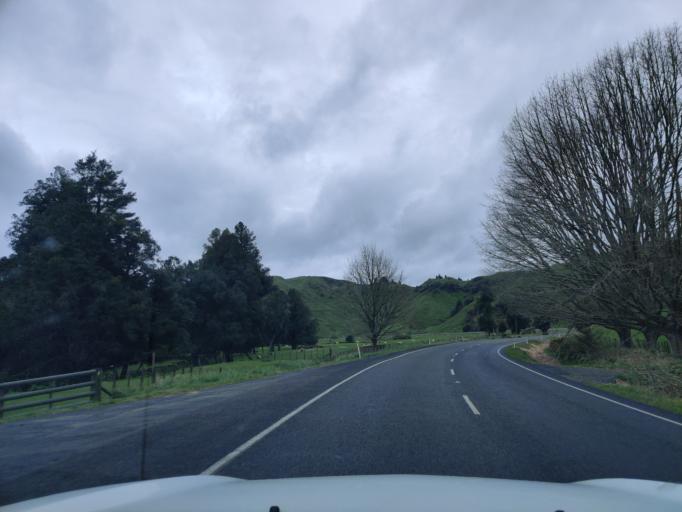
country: NZ
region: Waikato
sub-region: Otorohanga District
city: Otorohanga
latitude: -38.5560
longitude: 175.1948
